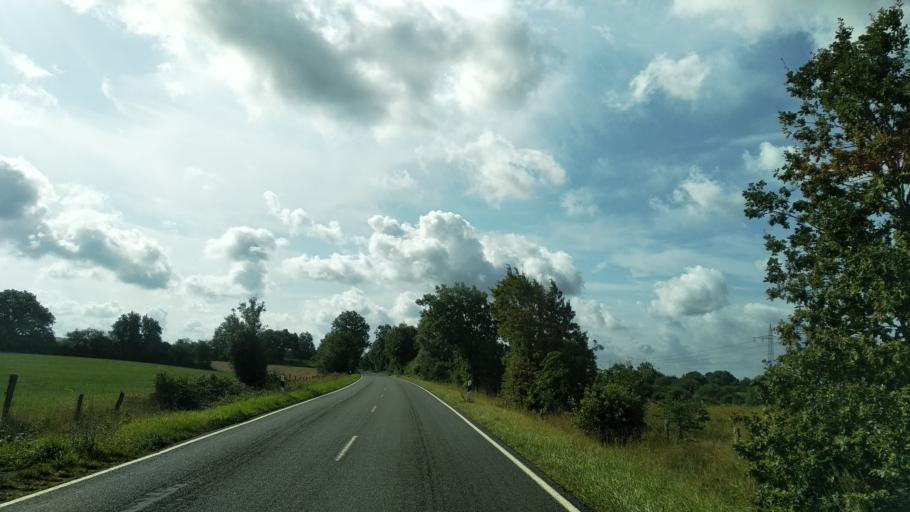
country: DE
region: Schleswig-Holstein
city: Geltorf
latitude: 54.4431
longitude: 9.5969
